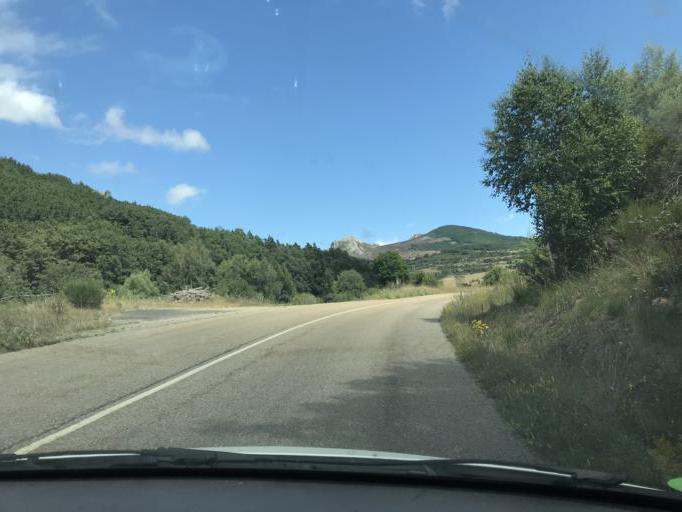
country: ES
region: Castille and Leon
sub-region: Provincia de Palencia
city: Polentinos
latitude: 42.9836
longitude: -4.4958
